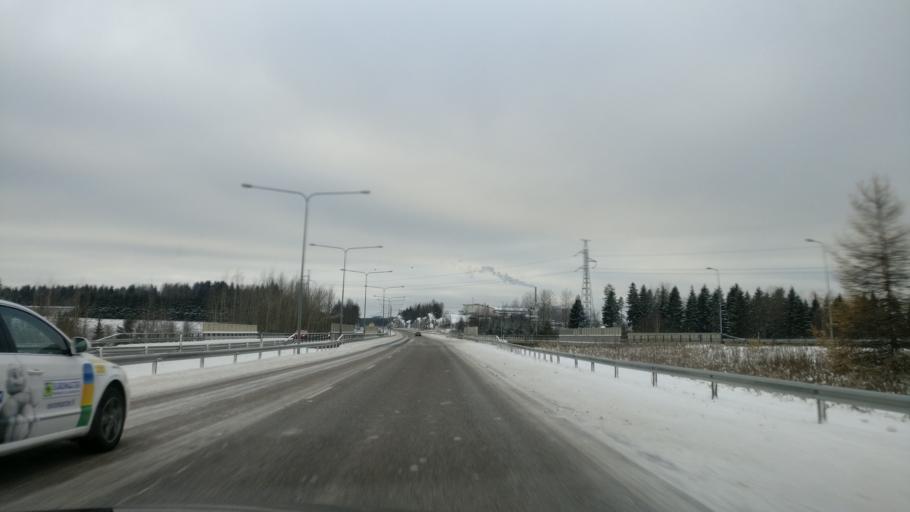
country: FI
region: Paijanne Tavastia
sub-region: Lahti
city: Lahti
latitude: 60.9686
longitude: 25.7154
